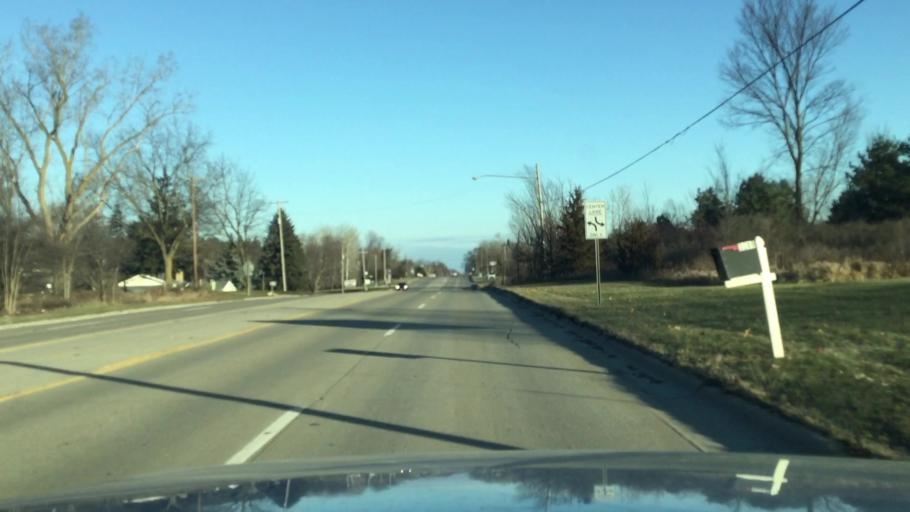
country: US
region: Michigan
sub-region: Genesee County
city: Flushing
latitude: 43.0535
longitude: -83.7727
